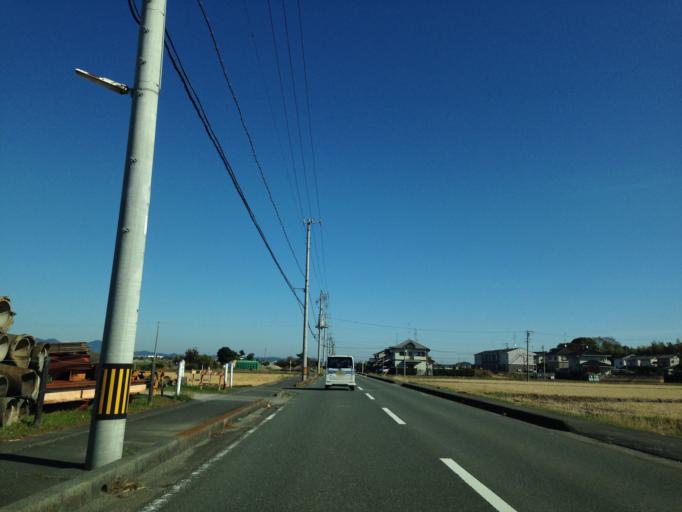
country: JP
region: Shizuoka
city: Fukuroi
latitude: 34.7529
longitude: 137.9445
